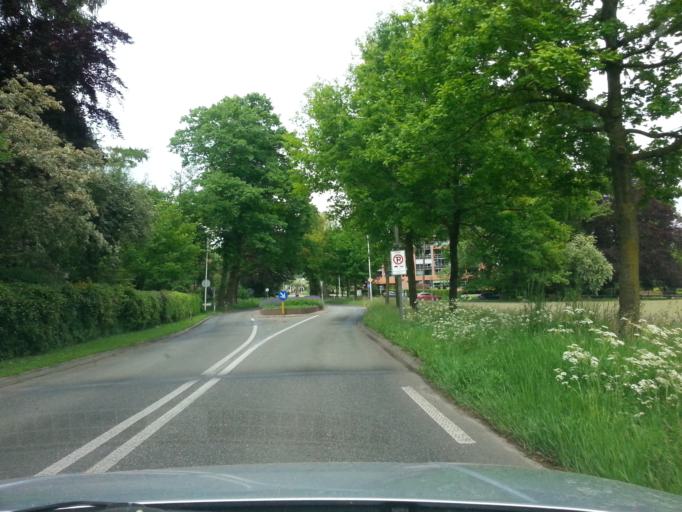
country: NL
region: Gelderland
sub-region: Gemeente Lochem
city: Lochem
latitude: 52.1481
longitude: 6.4197
